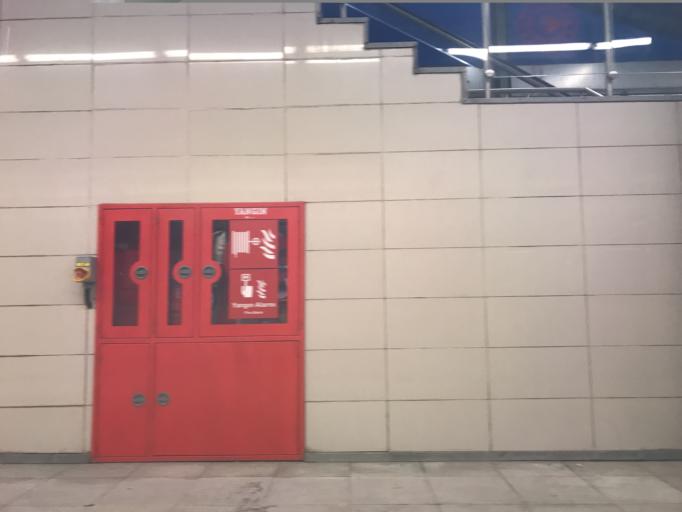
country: TR
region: Kocaeli
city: Darica
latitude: 40.7916
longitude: 29.3917
